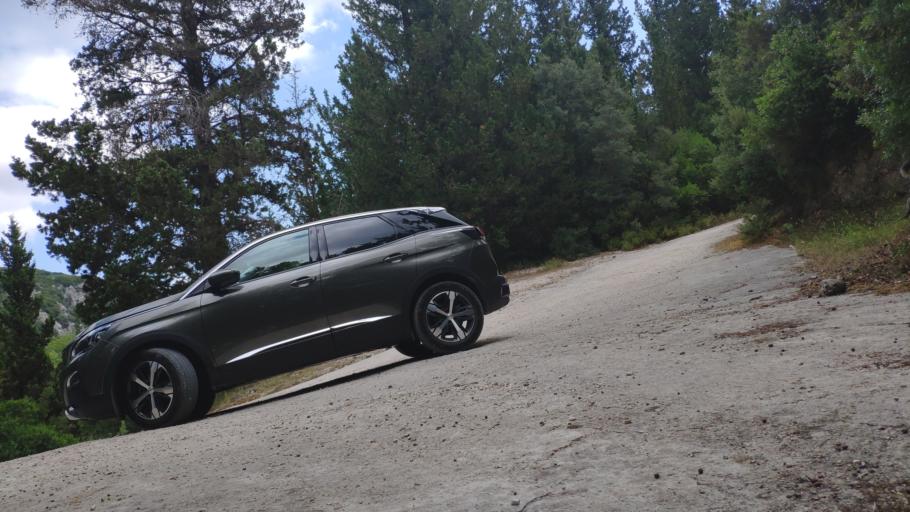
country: GR
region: Ionian Islands
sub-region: Lefkada
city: Lefkada
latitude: 38.8019
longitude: 20.6716
